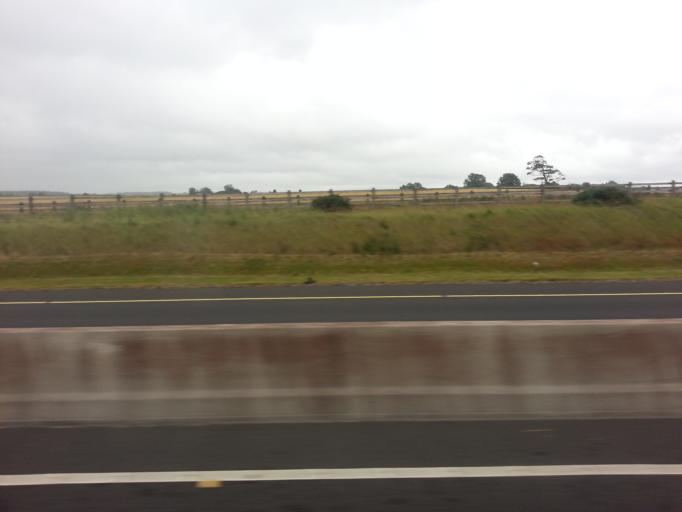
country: IE
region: Leinster
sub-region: Kildare
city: Moone
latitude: 52.9595
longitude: -6.8576
